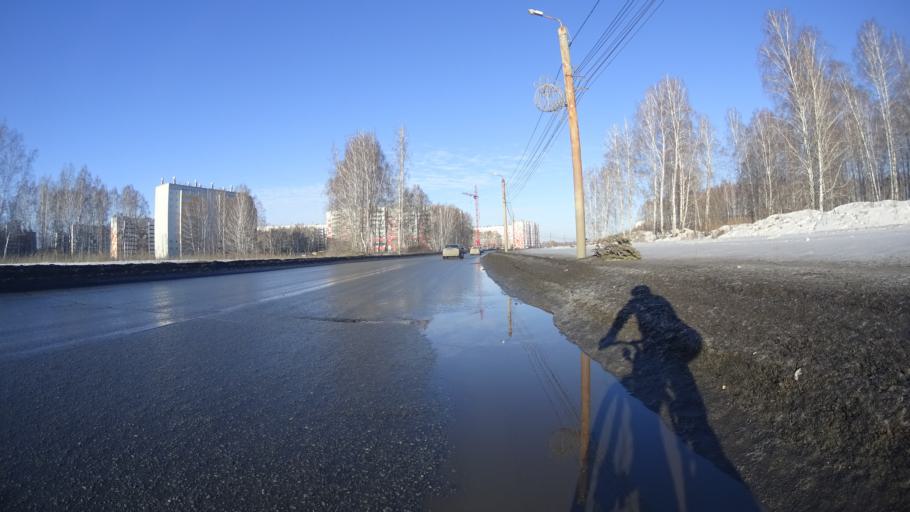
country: RU
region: Chelyabinsk
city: Roshchino
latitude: 55.2145
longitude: 61.2852
